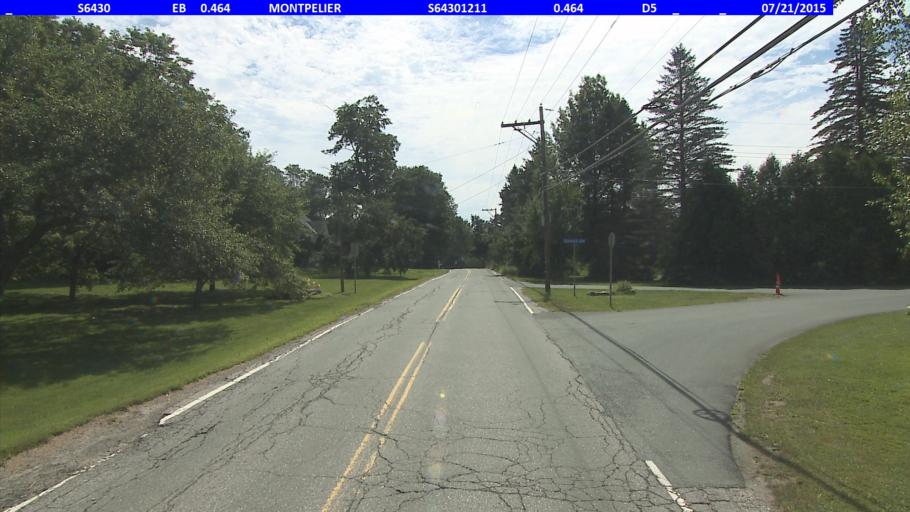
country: US
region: Vermont
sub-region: Washington County
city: Montpelier
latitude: 44.2589
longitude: -72.5504
